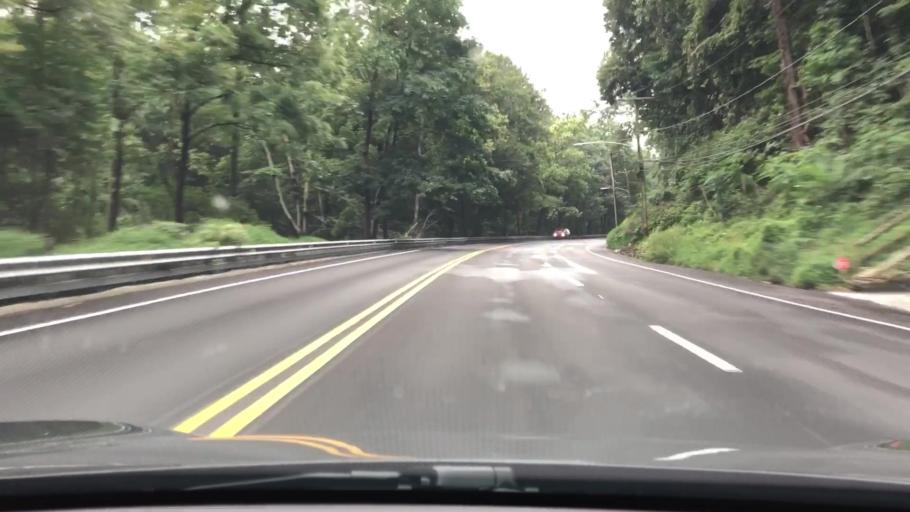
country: US
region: Pennsylvania
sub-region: Delaware County
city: Broomall
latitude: 39.9930
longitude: -75.3561
